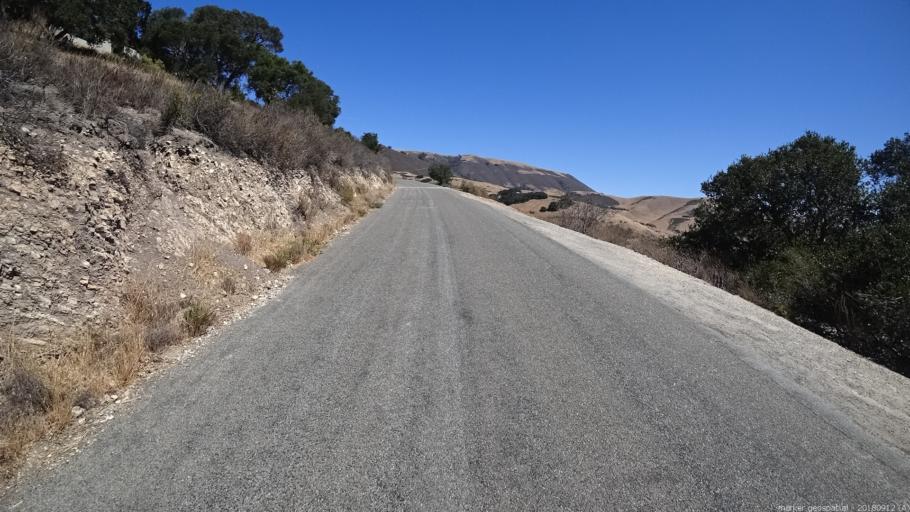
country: US
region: California
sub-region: Monterey County
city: Carmel Valley Village
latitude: 36.4838
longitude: -121.7216
